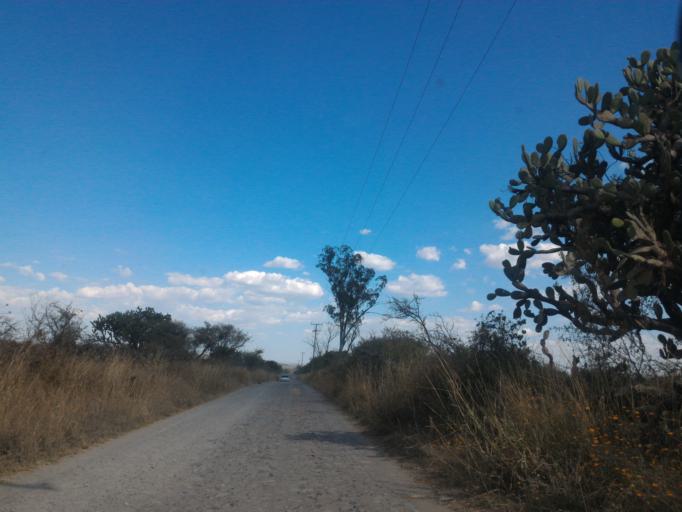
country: MX
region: Jalisco
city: San Diego de Alejandria
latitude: 20.8835
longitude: -102.0018
